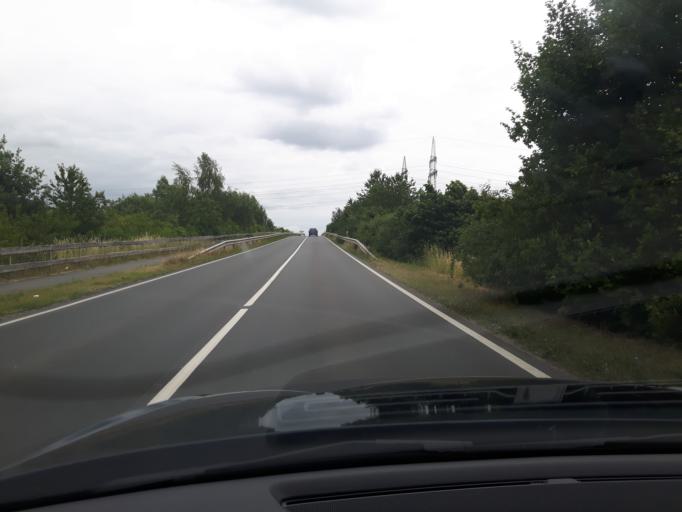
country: DE
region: Lower Saxony
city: Lehrte
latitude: 52.3824
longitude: 9.9465
